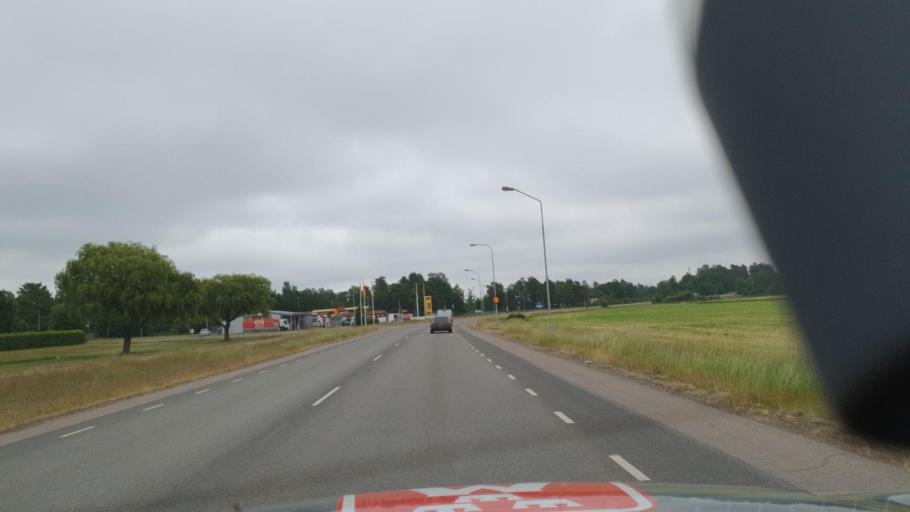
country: SE
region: Kalmar
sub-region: Kalmar Kommun
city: Lindsdal
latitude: 56.7238
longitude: 16.2986
